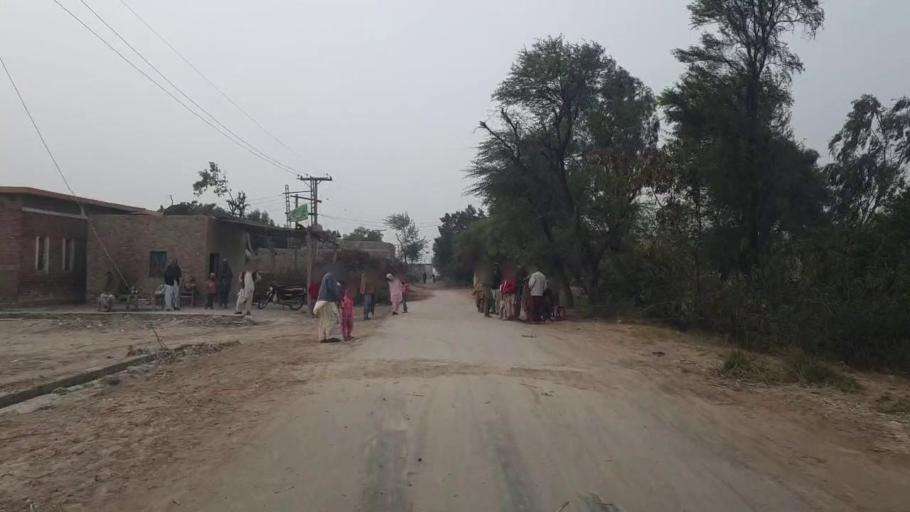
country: PK
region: Sindh
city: Shahdadpur
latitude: 25.8724
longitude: 68.6287
